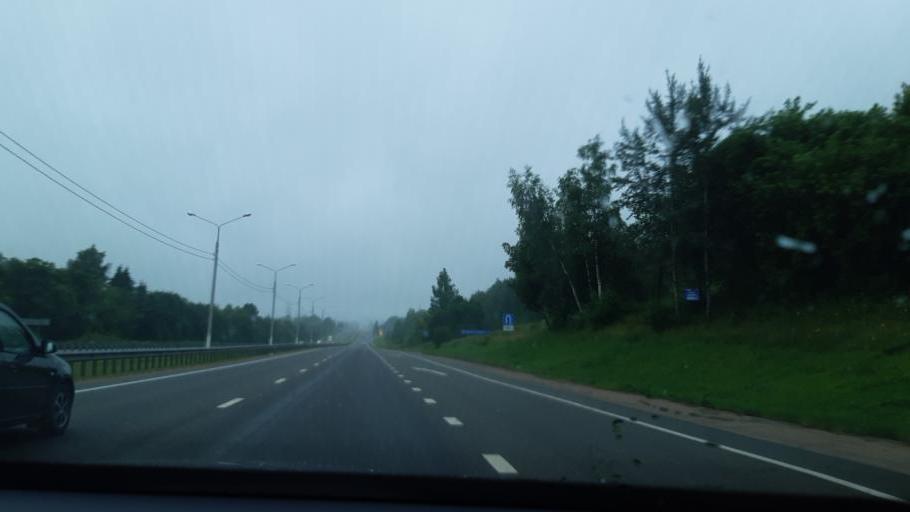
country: RU
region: Smolensk
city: Talashkino
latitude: 54.6509
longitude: 32.1679
